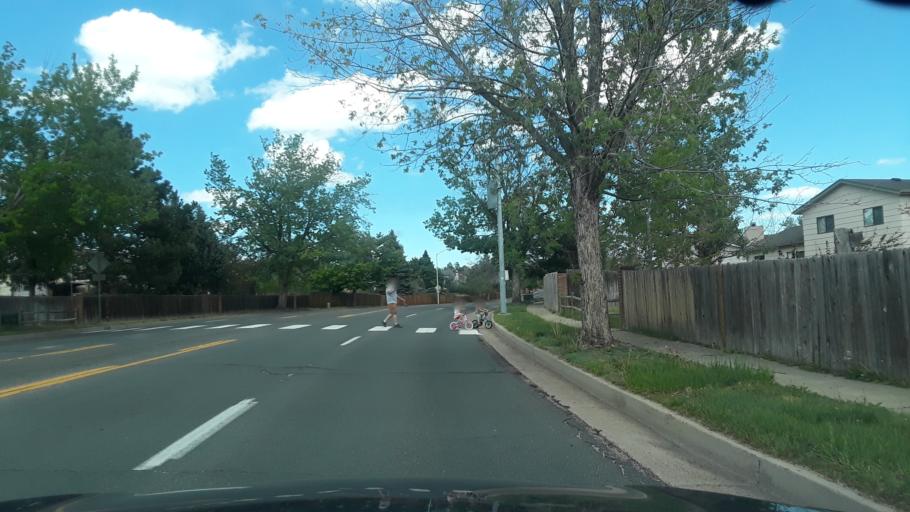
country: US
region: Colorado
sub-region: El Paso County
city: Black Forest
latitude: 38.9430
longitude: -104.7596
